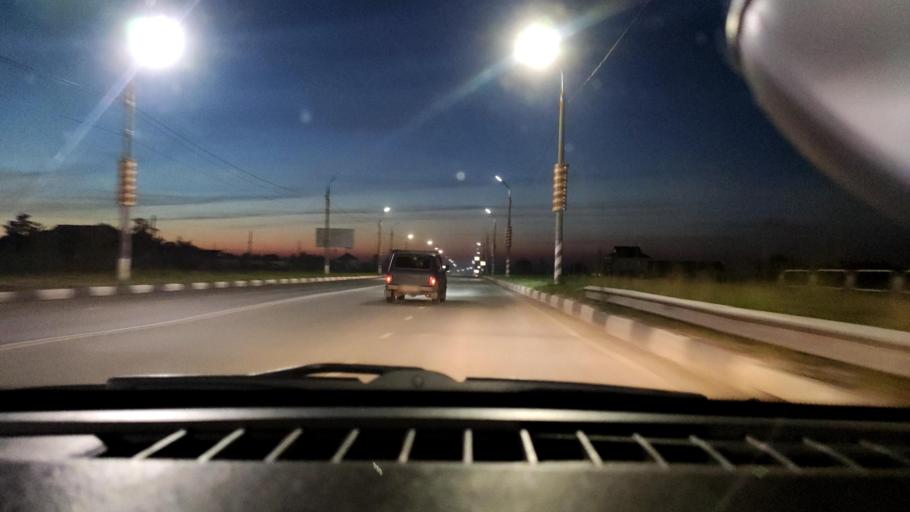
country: RU
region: Samara
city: Novokuybyshevsk
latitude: 53.0756
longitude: 49.9973
